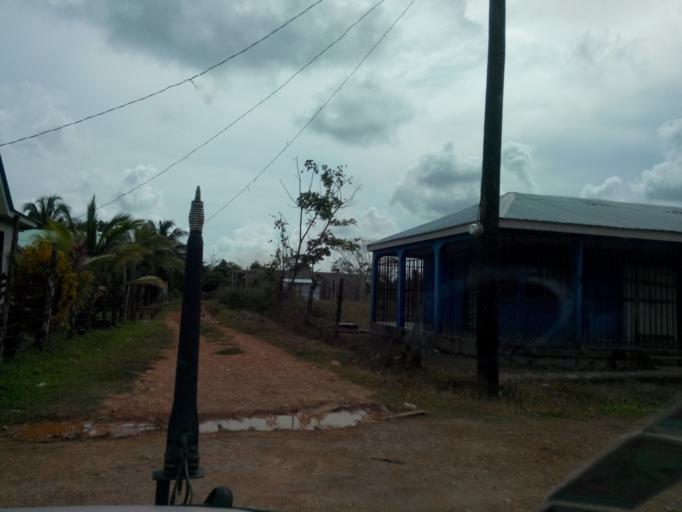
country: NI
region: Atlantico Sur
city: Bluefields
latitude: 12.0021
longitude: -83.7689
